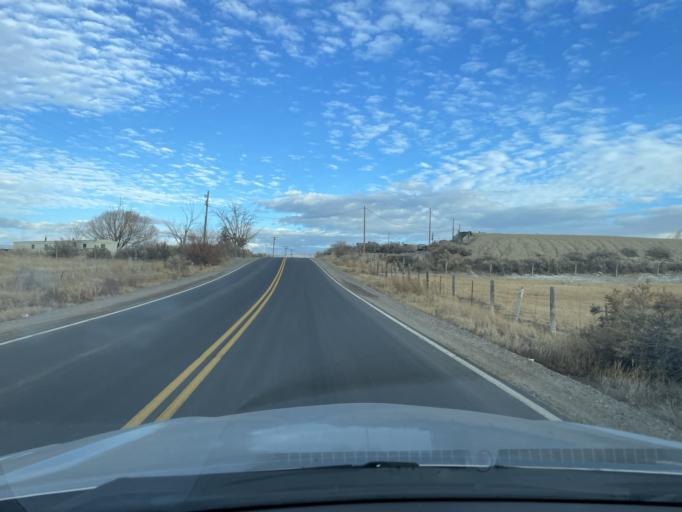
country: US
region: Colorado
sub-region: Montrose County
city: Olathe
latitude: 38.6351
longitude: -107.9901
